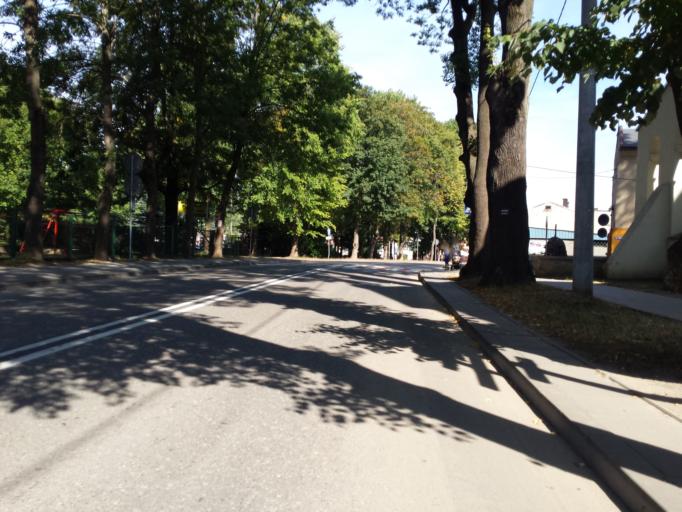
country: PL
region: Subcarpathian Voivodeship
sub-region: Powiat leski
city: Baligrod
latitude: 49.3360
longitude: 22.2870
